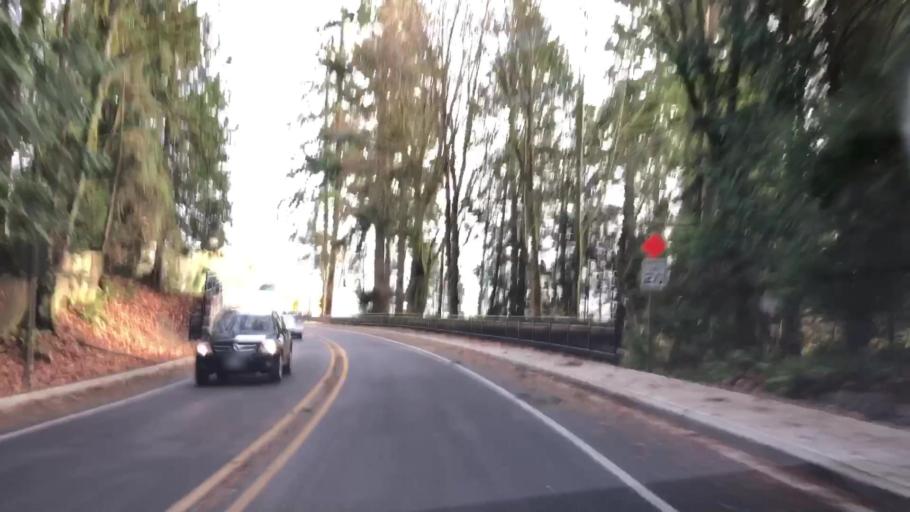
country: US
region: Washington
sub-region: Kitsap County
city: Suquamish
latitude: 47.7288
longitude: -122.5553
